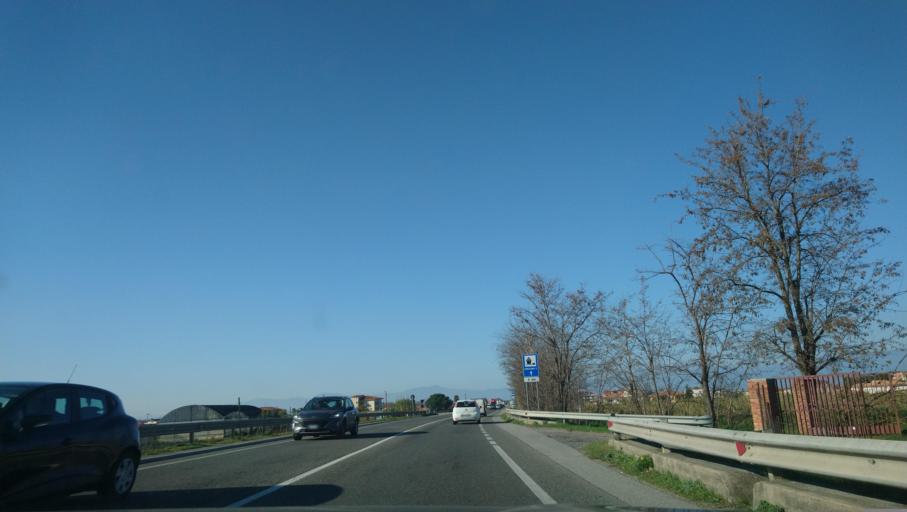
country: IT
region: Calabria
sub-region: Provincia di Cosenza
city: Fabrizio
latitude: 39.6335
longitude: 16.5530
